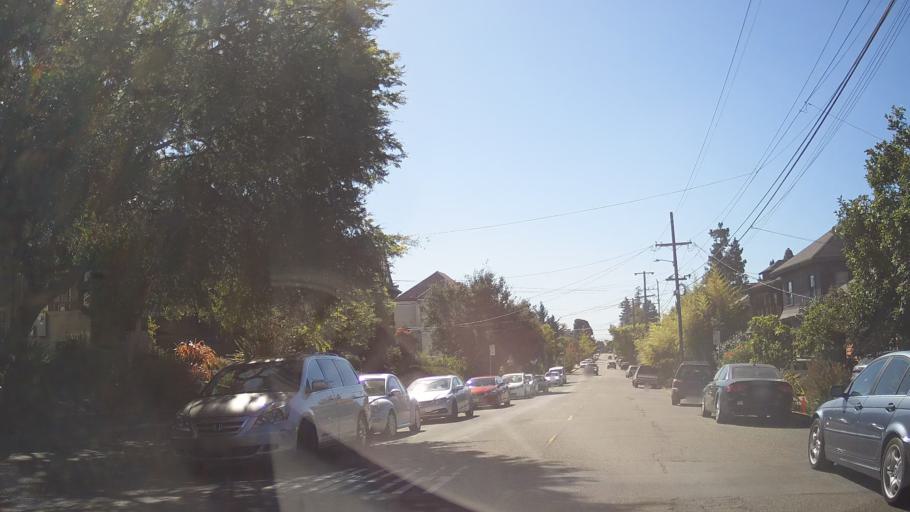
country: US
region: California
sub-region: Alameda County
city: Berkeley
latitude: 37.8834
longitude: -122.2675
